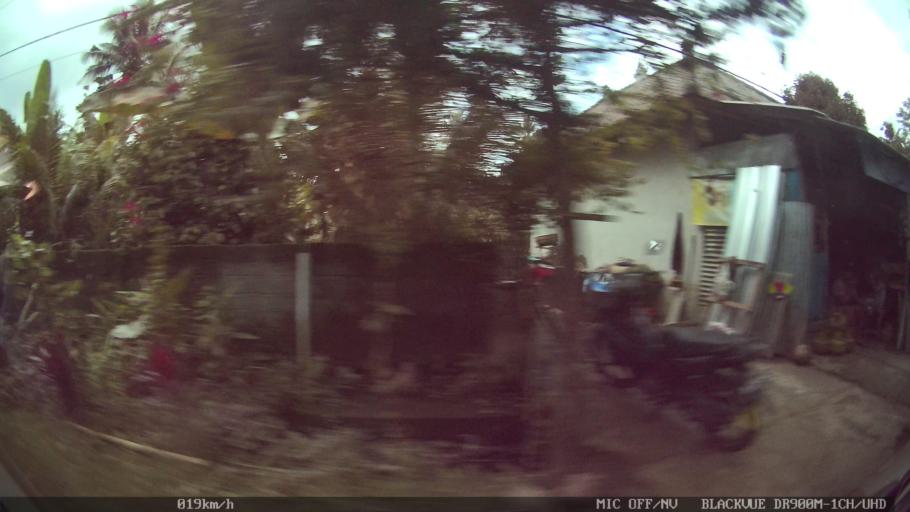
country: ID
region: Bali
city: Banjar Wangsian
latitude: -8.4521
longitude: 115.4199
